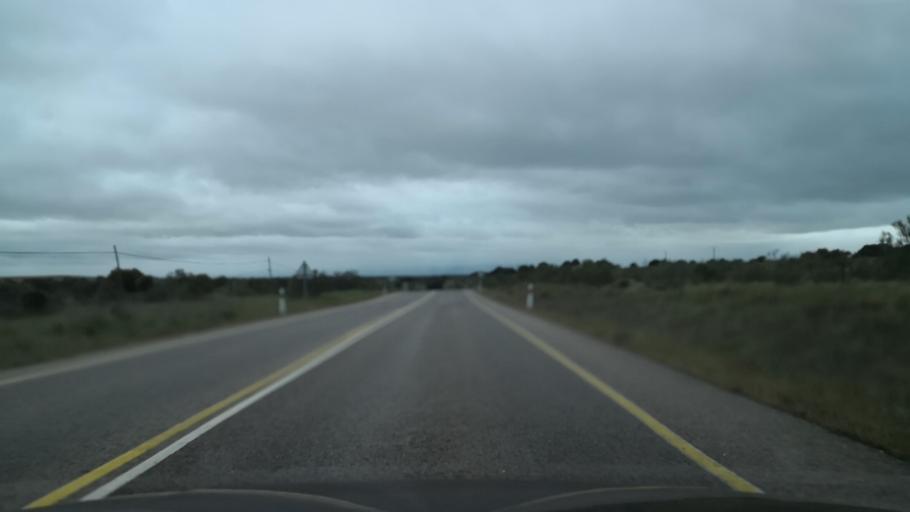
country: ES
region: Extremadura
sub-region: Provincia de Caceres
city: Caceres
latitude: 39.4226
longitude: -6.4123
